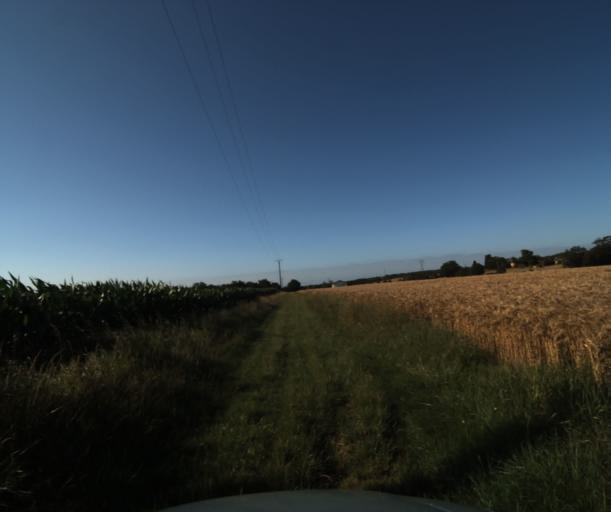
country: FR
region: Midi-Pyrenees
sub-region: Departement de la Haute-Garonne
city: Labarthe-sur-Leze
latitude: 43.4423
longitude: 1.3766
